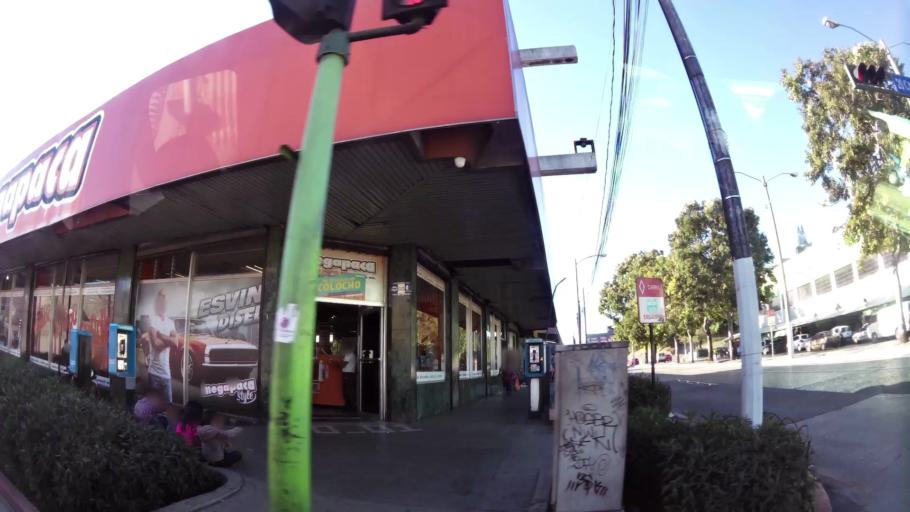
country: GT
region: Guatemala
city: Guatemala City
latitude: 14.6294
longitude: -90.5157
